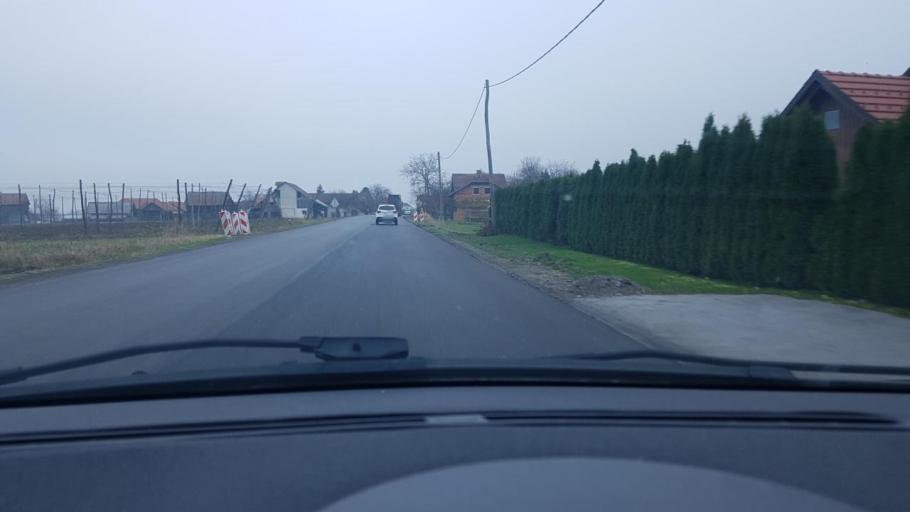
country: SI
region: Tabor
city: Tabor
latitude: 46.2482
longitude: 15.0250
